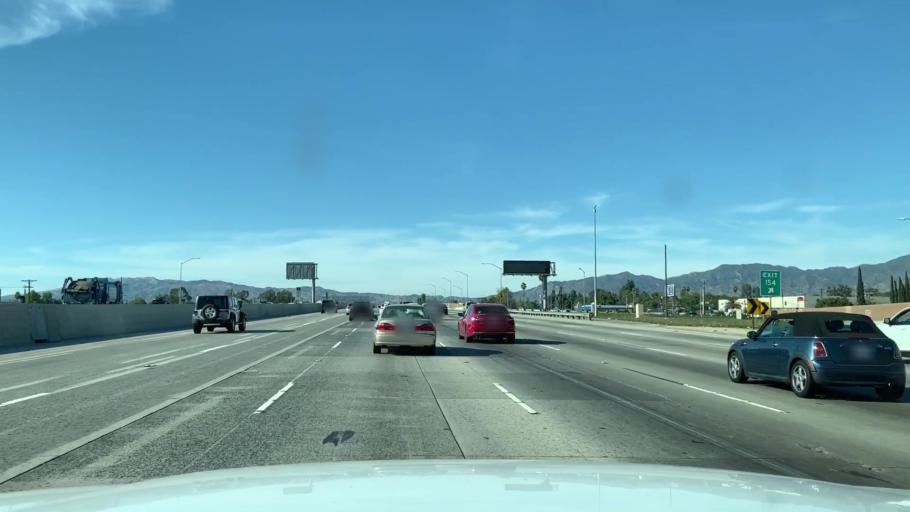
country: US
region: California
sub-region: Los Angeles County
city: San Fernando
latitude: 34.2432
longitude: -118.4206
